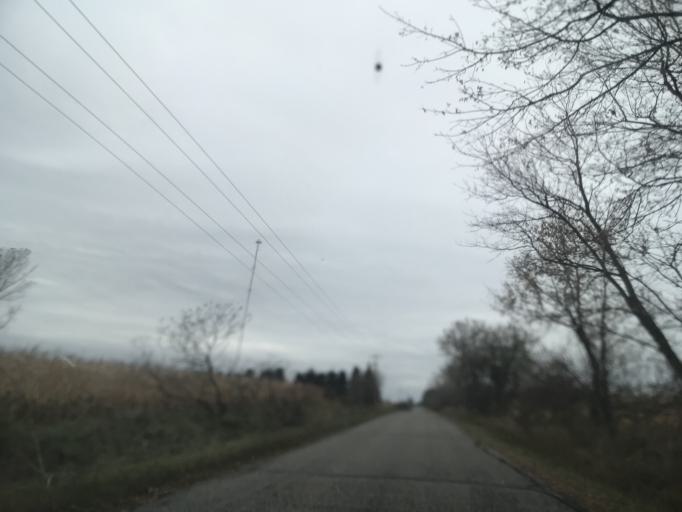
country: US
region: Wisconsin
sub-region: Menominee County
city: Legend Lake
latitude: 45.1742
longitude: -88.4555
